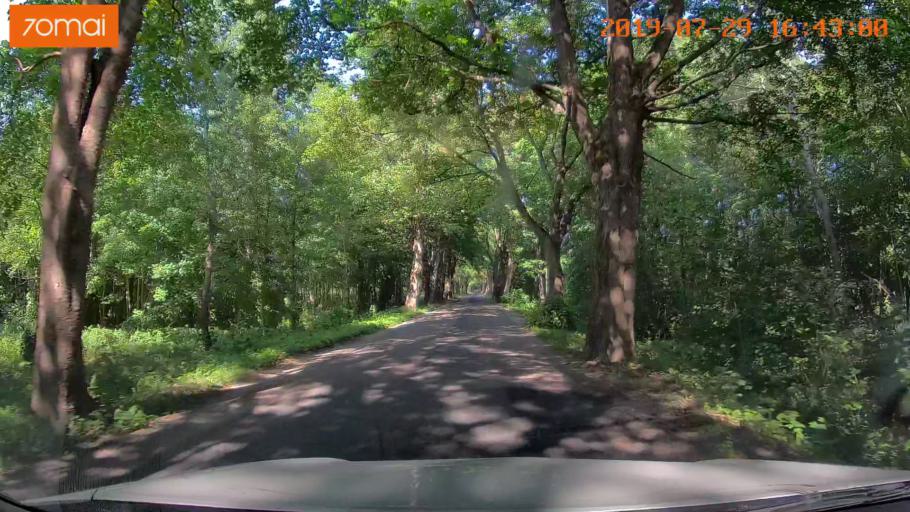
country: RU
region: Kaliningrad
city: Primorsk
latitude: 54.7462
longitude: 20.0794
